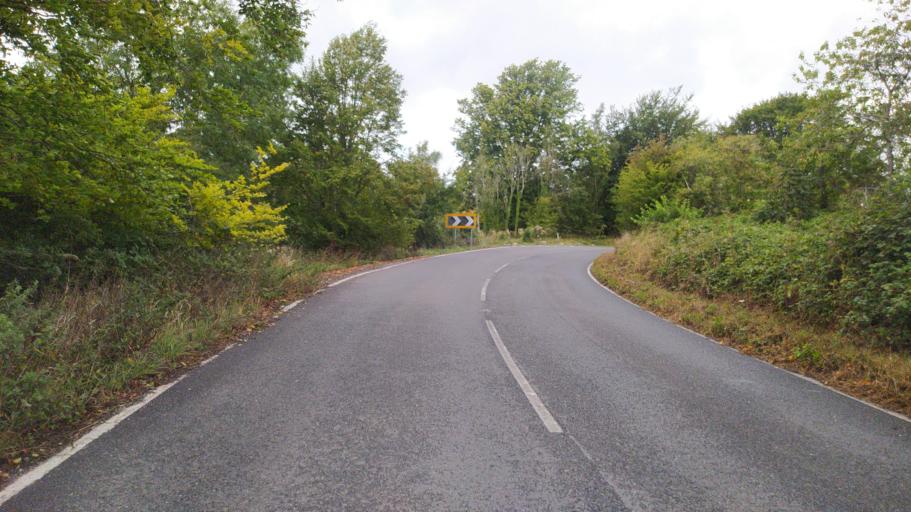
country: GB
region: England
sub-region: Hampshire
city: Petersfield
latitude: 50.9564
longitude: -0.8766
